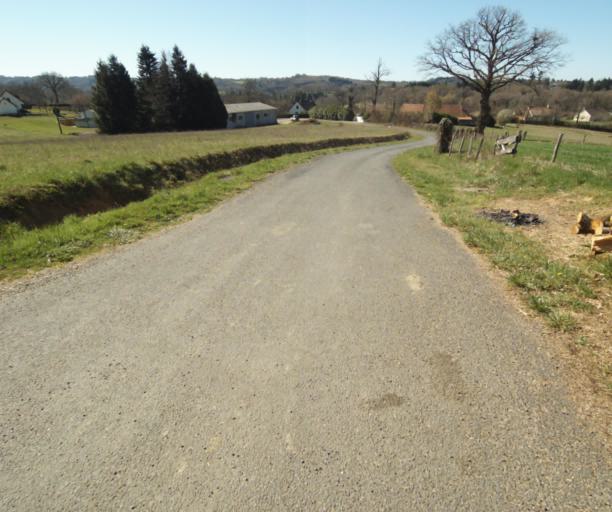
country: FR
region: Limousin
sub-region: Departement de la Correze
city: Chamboulive
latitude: 45.4307
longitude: 1.7183
